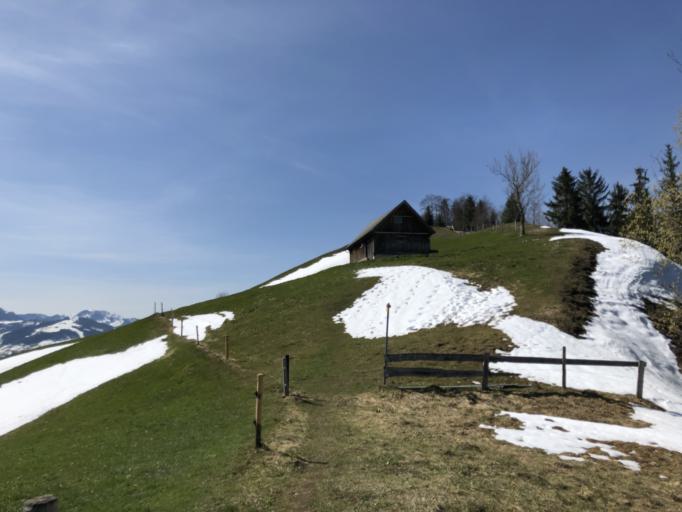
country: CH
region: Appenzell Innerrhoden
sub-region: Appenzell Inner Rhodes
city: Gonten
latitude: 47.3426
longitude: 9.3675
